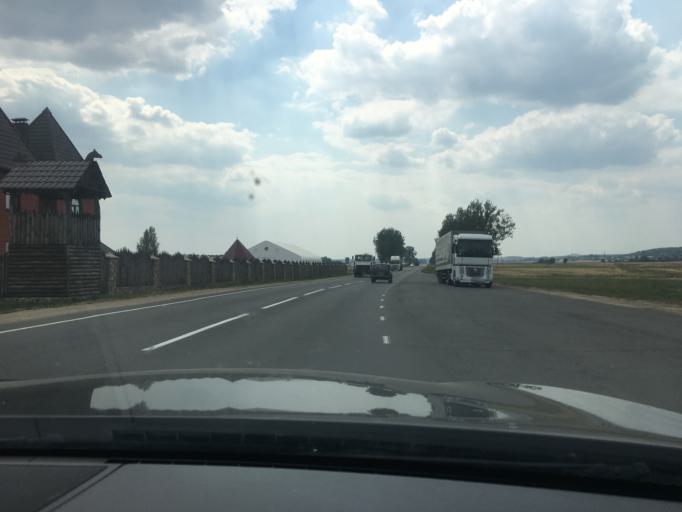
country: BY
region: Brest
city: Ruzhany
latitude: 52.8593
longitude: 24.8896
